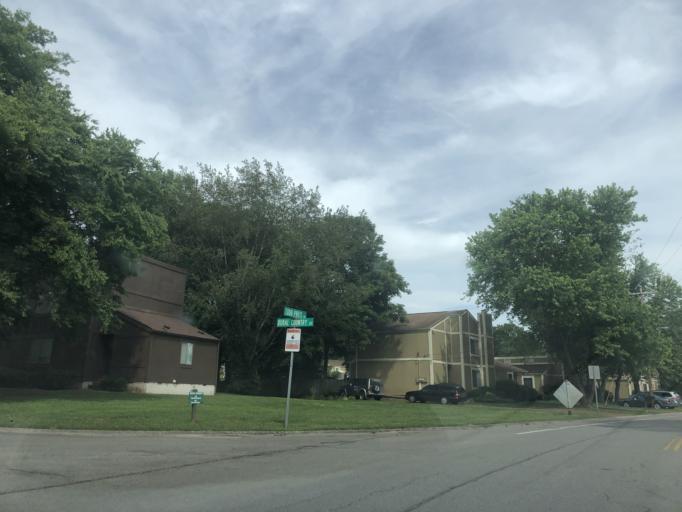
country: US
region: Tennessee
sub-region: Davidson County
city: Belle Meade
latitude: 36.0703
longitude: -86.9454
